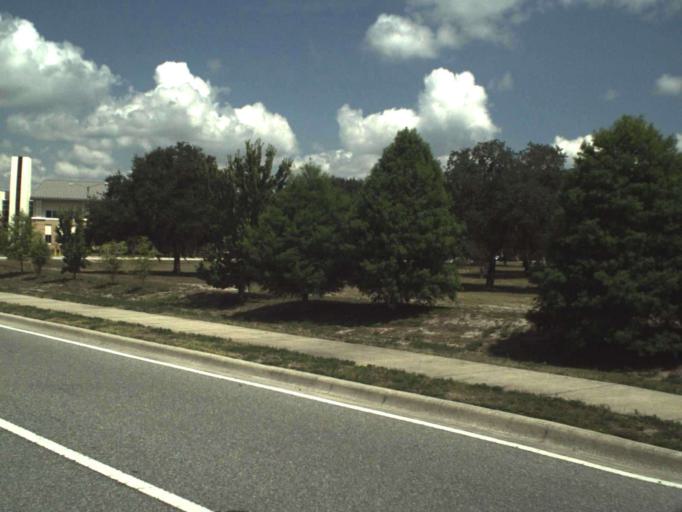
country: US
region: Florida
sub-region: Lake County
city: Silver Lake
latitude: 28.8253
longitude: -81.7938
